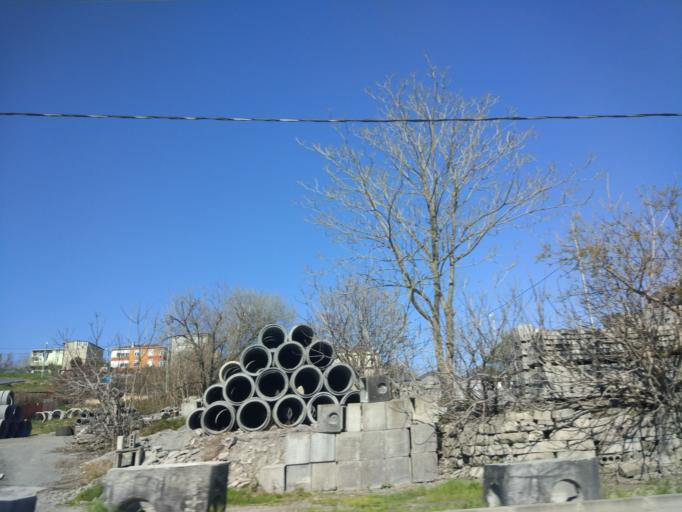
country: TR
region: Istanbul
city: Basaksehir
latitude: 41.0432
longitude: 28.7546
